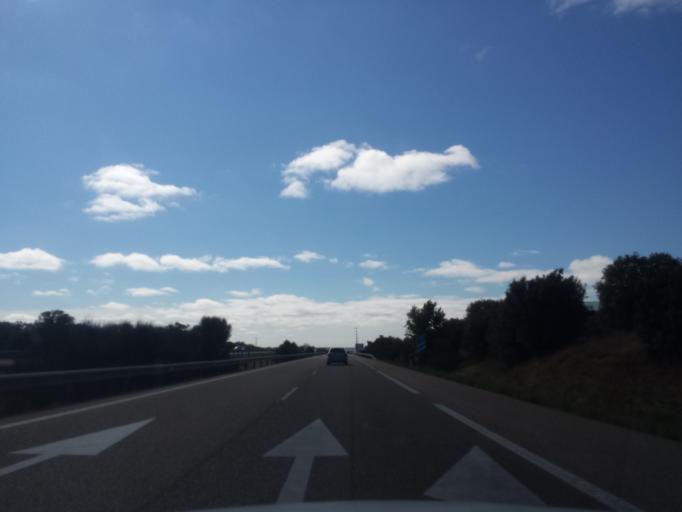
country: ES
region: Castille and Leon
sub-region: Provincia de Valladolid
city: San Pedro de Latarce
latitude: 41.7796
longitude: -5.3179
